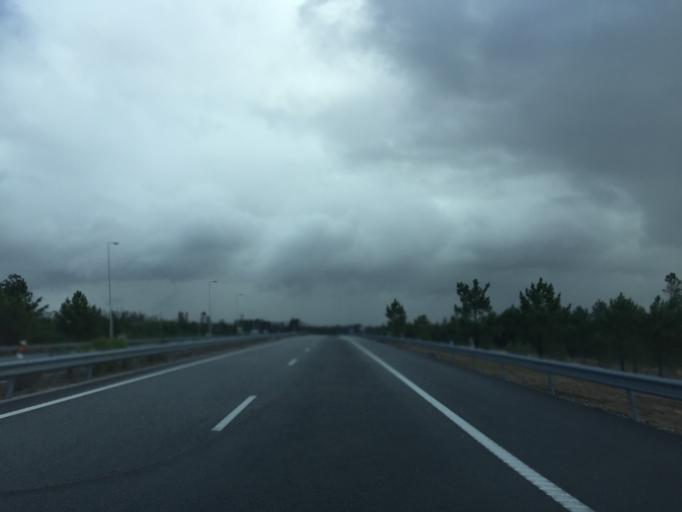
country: PT
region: Coimbra
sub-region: Cantanhede
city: Cantanhede
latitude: 40.2850
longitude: -8.5271
